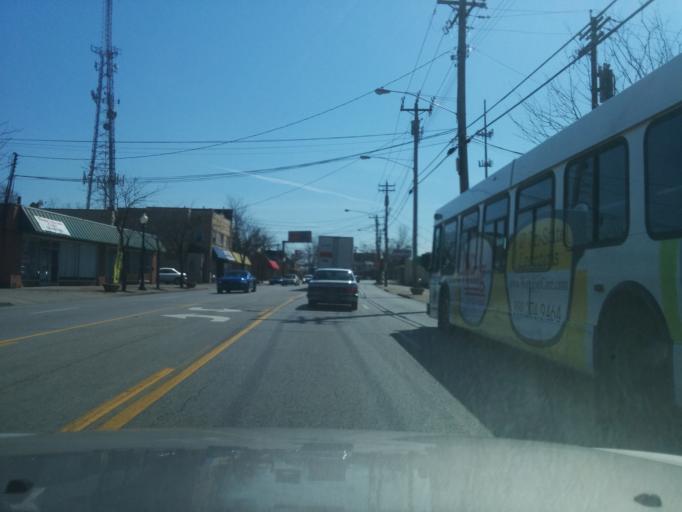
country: US
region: Ohio
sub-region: Hamilton County
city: Monfort Heights
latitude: 39.1931
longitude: -84.5724
